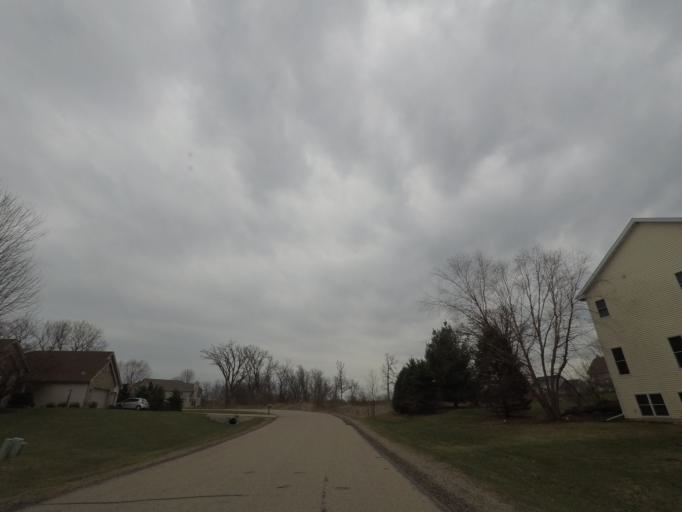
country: US
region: Wisconsin
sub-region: Dane County
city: Middleton
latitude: 43.1153
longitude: -89.5669
